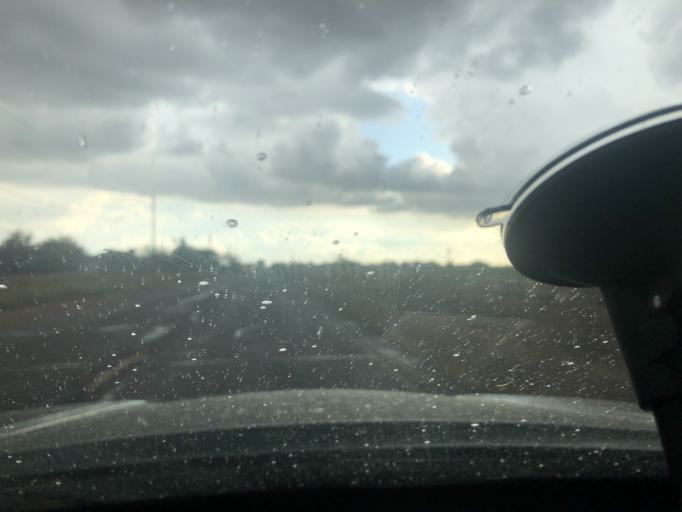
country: US
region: Arizona
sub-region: Maricopa County
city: Scottsdale
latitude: 33.4828
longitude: -111.8827
